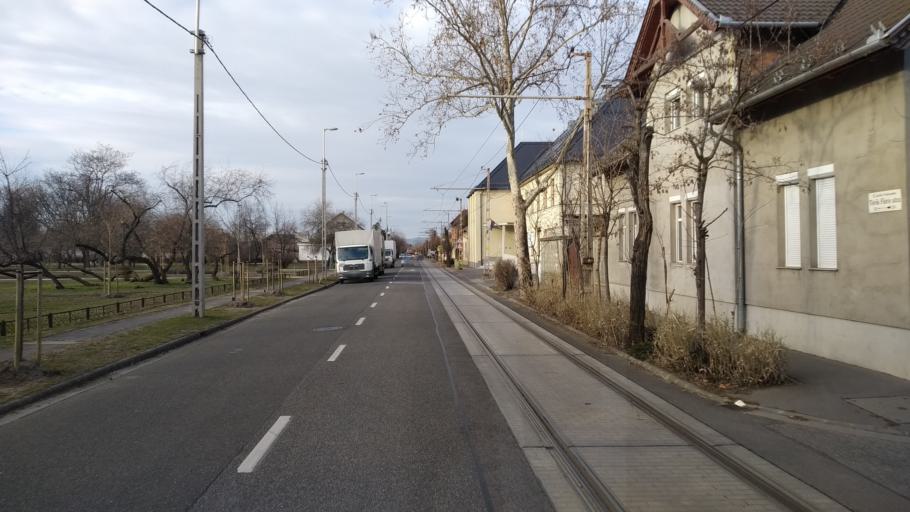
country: HU
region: Budapest
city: Budapest XX. keruelet
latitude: 47.4265
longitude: 19.1212
